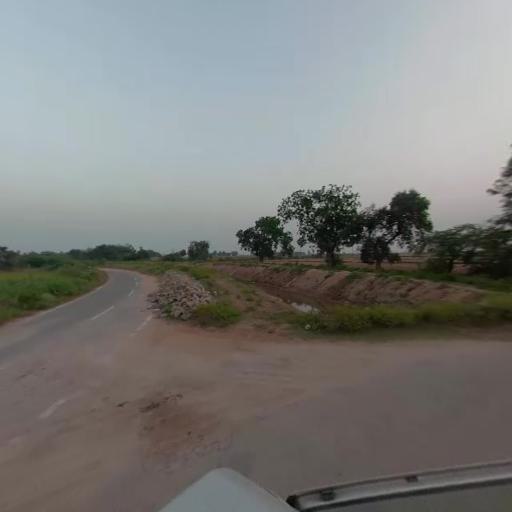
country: IN
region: Telangana
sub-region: Nalgonda
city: Suriapet
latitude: 17.1139
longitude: 79.5289
